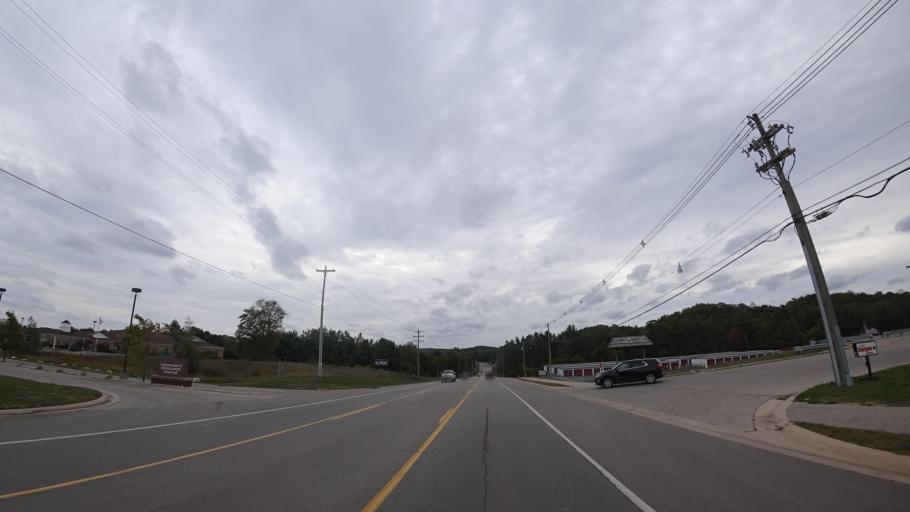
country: US
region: Michigan
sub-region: Emmet County
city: Petoskey
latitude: 45.4200
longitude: -84.9045
